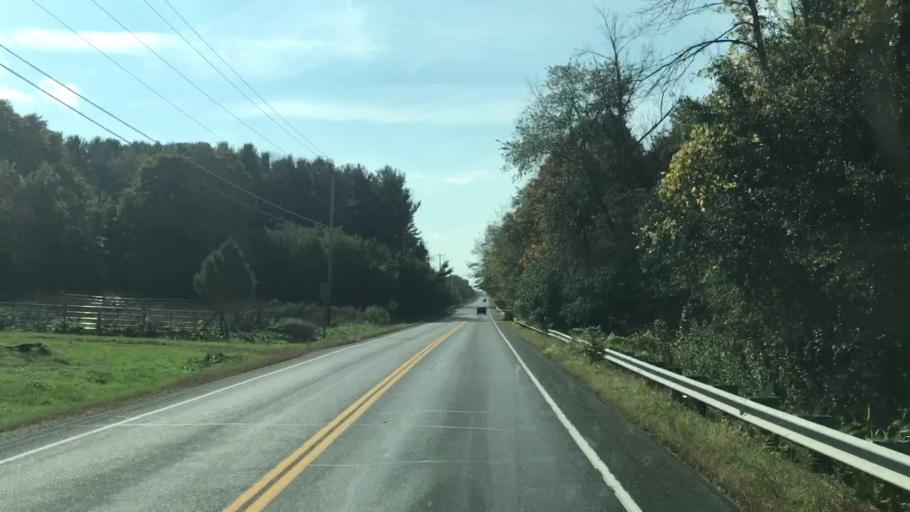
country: US
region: Wisconsin
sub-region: Ozaukee County
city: Mequon
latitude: 43.2205
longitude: -88.0435
